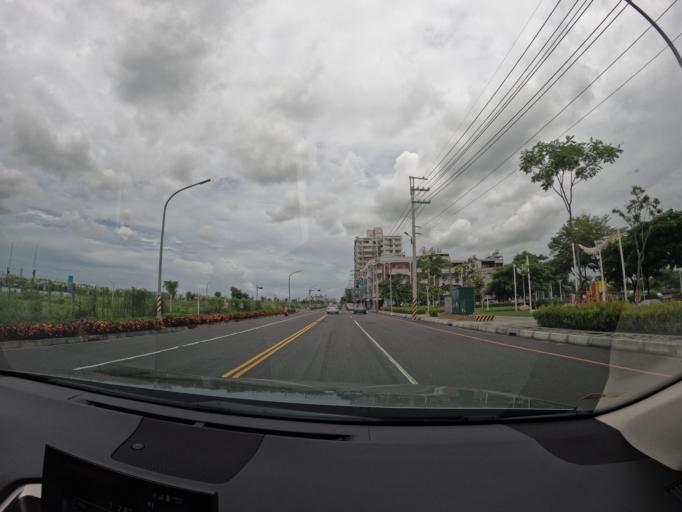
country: TW
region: Kaohsiung
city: Kaohsiung
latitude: 22.7845
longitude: 120.2941
